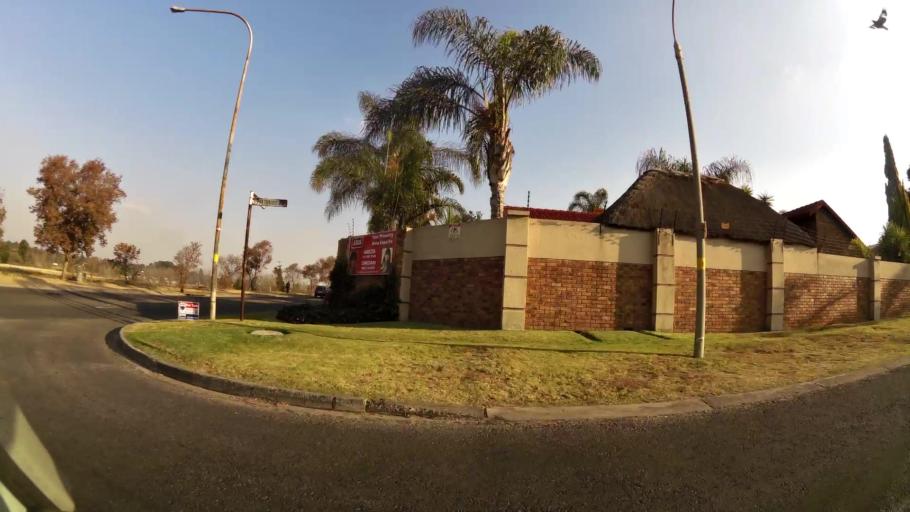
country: ZA
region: Gauteng
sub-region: City of Johannesburg Metropolitan Municipality
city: Modderfontein
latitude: -26.0742
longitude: 28.2247
